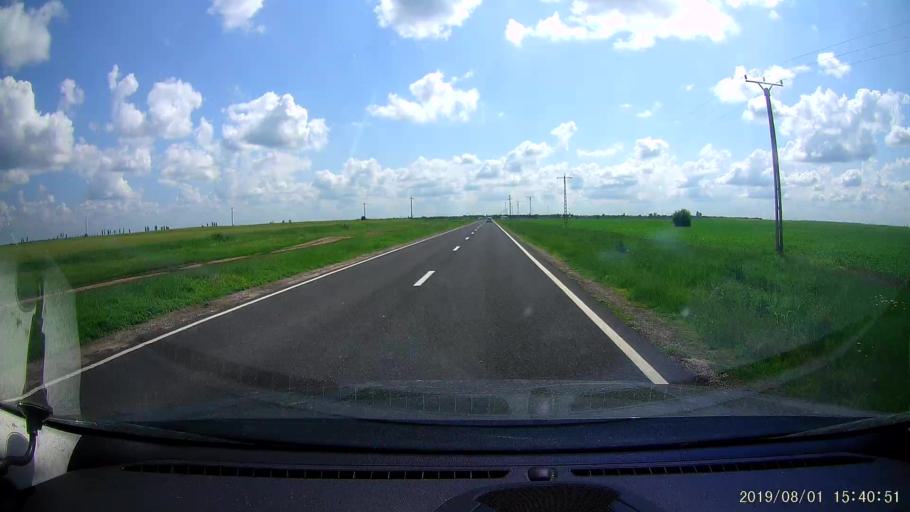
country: RO
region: Braila
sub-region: Comuna Baraganul
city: Baraganul
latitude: 44.8309
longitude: 27.5360
